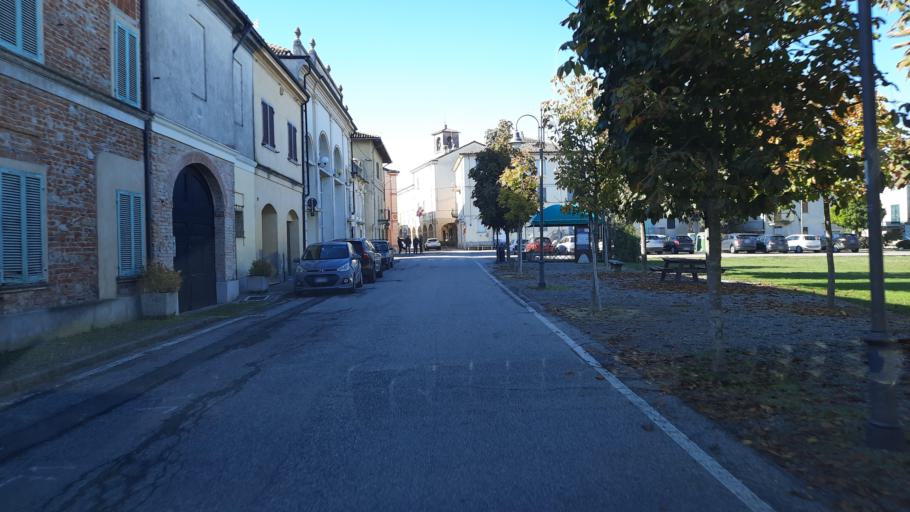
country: IT
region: Piedmont
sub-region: Provincia di Alessandria
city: Pontestura
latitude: 45.1437
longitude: 8.3340
